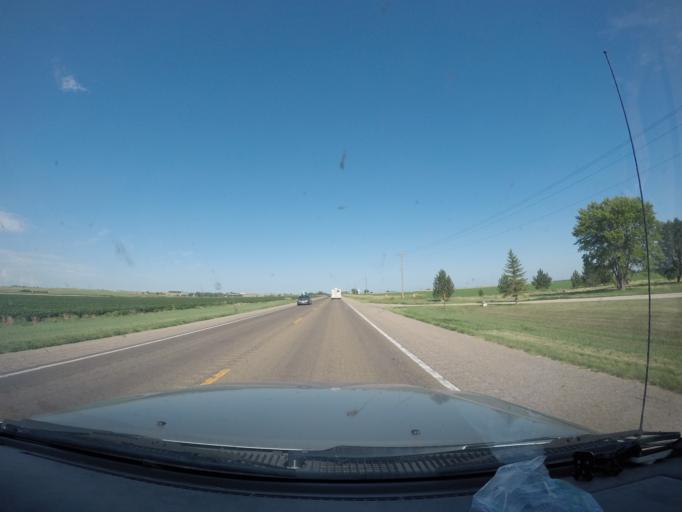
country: US
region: Nebraska
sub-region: Buffalo County
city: Kearney
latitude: 40.6996
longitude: -99.2088
